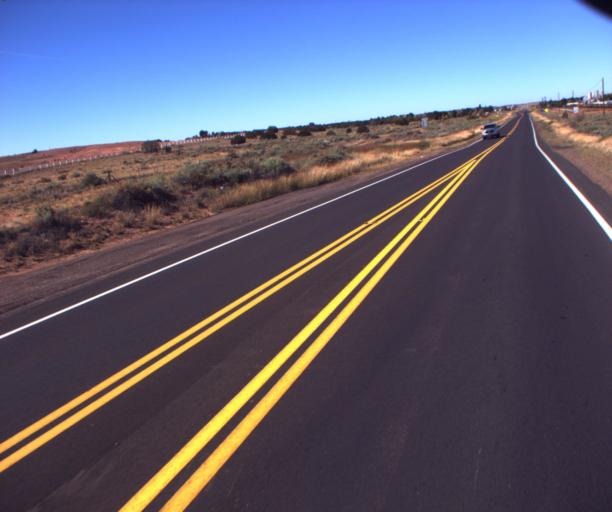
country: US
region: Arizona
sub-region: Navajo County
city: Snowflake
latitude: 34.5132
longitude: -110.0979
